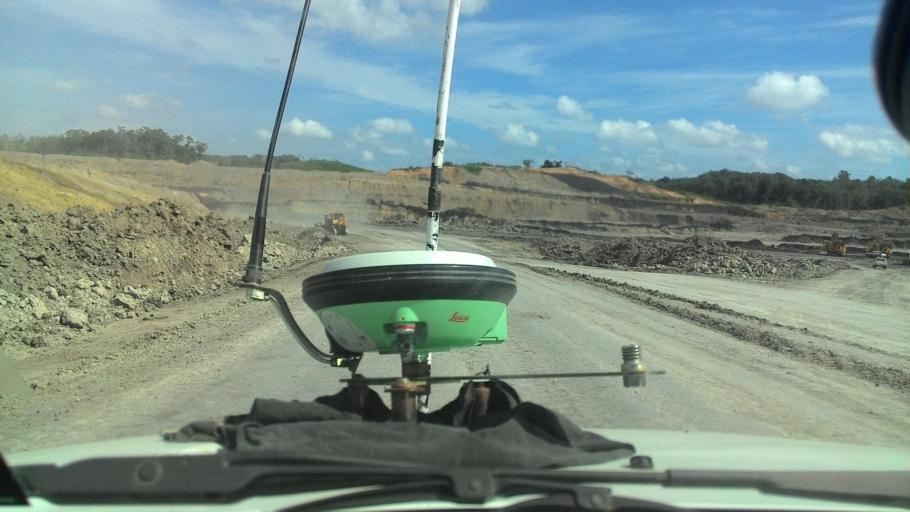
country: ID
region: South Kalimantan
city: Mungkuruyam
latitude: -2.1430
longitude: 115.5808
